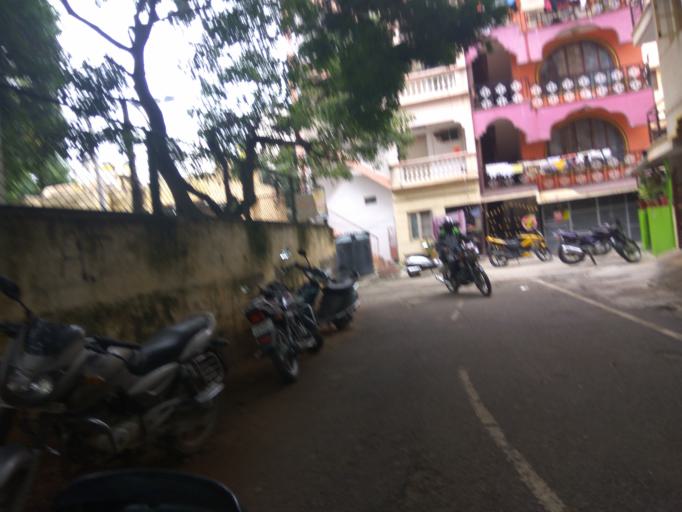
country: IN
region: Karnataka
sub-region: Bangalore Urban
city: Bangalore
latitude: 12.9658
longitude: 77.6603
